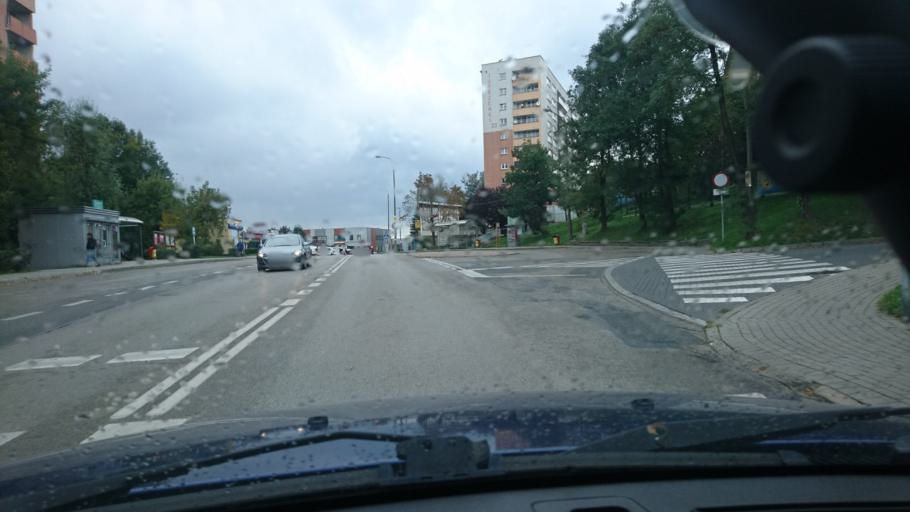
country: PL
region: Silesian Voivodeship
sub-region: Bielsko-Biala
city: Bielsko-Biala
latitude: 49.8058
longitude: 19.0624
